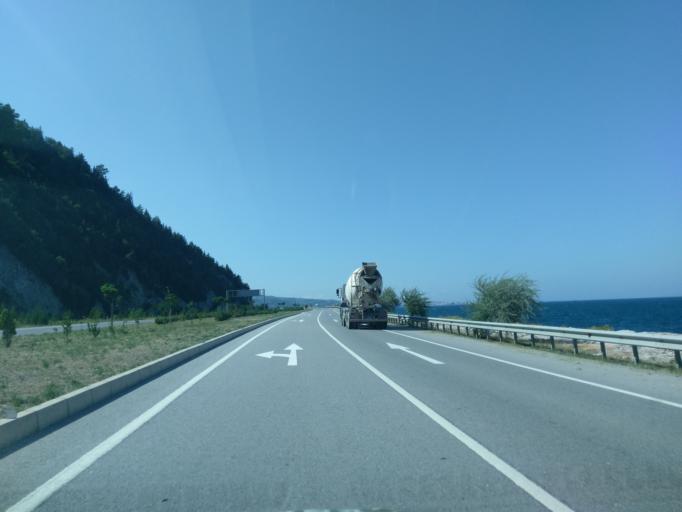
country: TR
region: Sinop
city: Gerze
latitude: 41.7479
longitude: 35.2427
